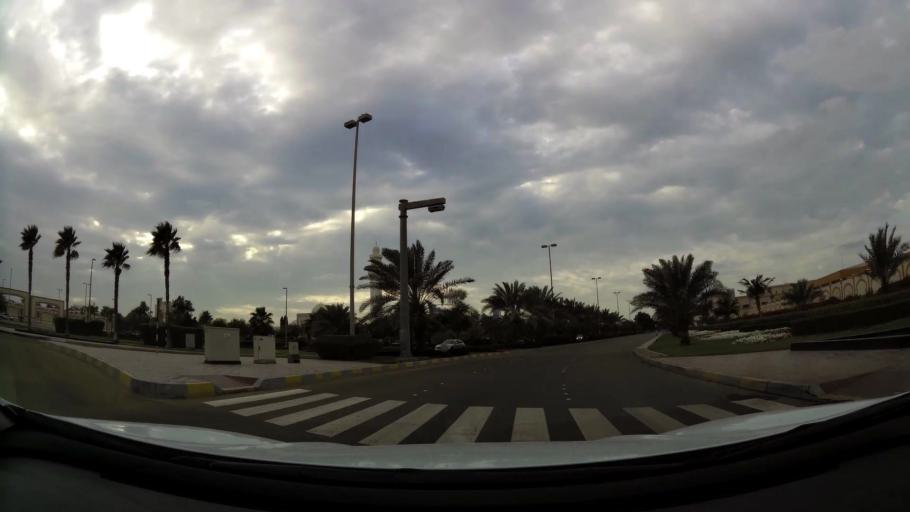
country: AE
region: Abu Dhabi
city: Abu Dhabi
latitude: 24.4480
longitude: 54.3544
